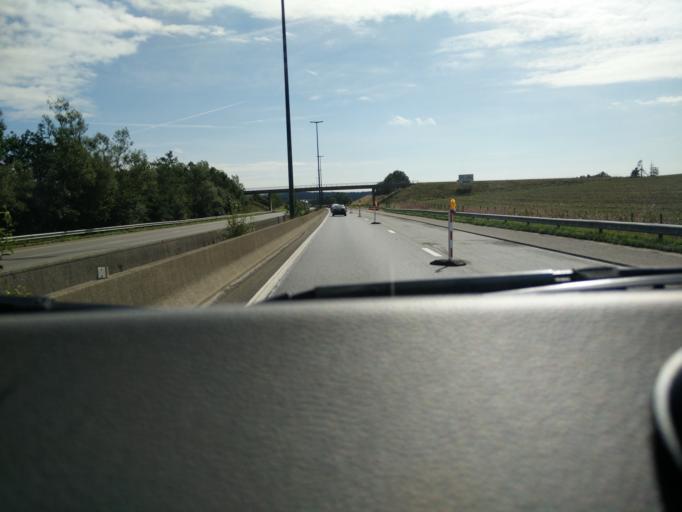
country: BE
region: Wallonia
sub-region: Province du Luxembourg
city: Neufchateau
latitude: 49.8915
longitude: 5.3494
